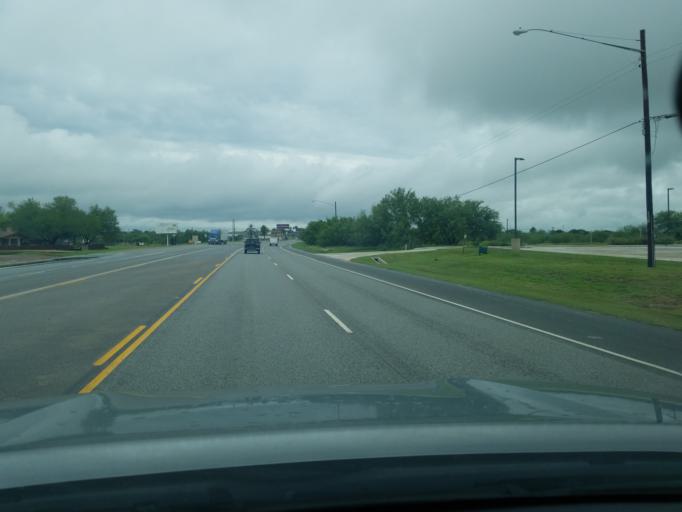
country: US
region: Texas
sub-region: Dimmit County
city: Carrizo Springs
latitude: 28.5374
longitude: -99.8503
